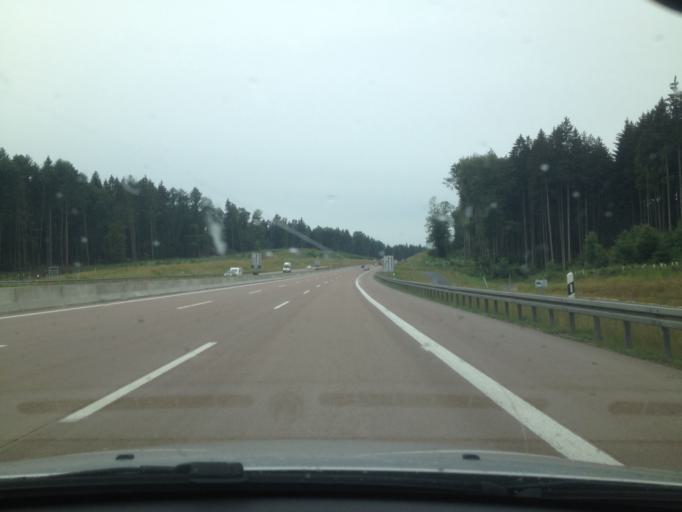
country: DE
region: Bavaria
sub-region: Swabia
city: Horgau
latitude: 48.4156
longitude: 10.6656
